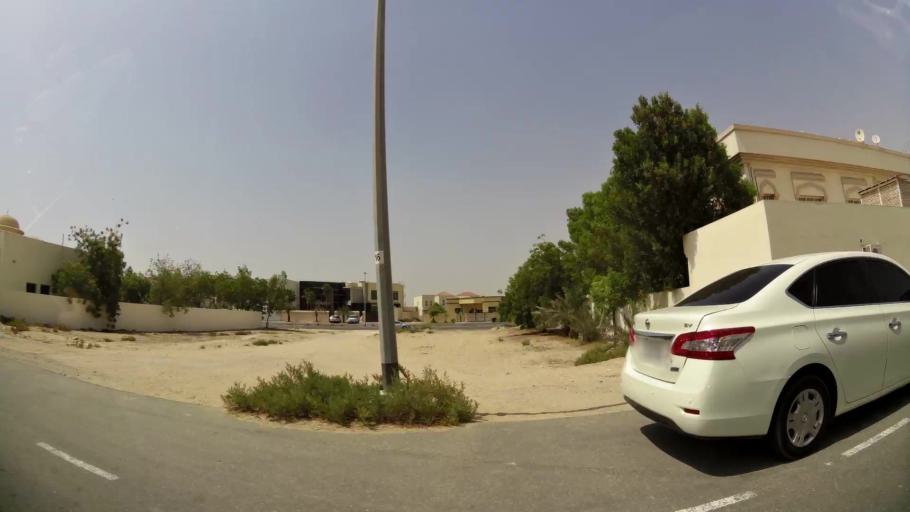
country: AE
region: Ash Shariqah
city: Sharjah
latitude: 25.2473
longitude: 55.4284
